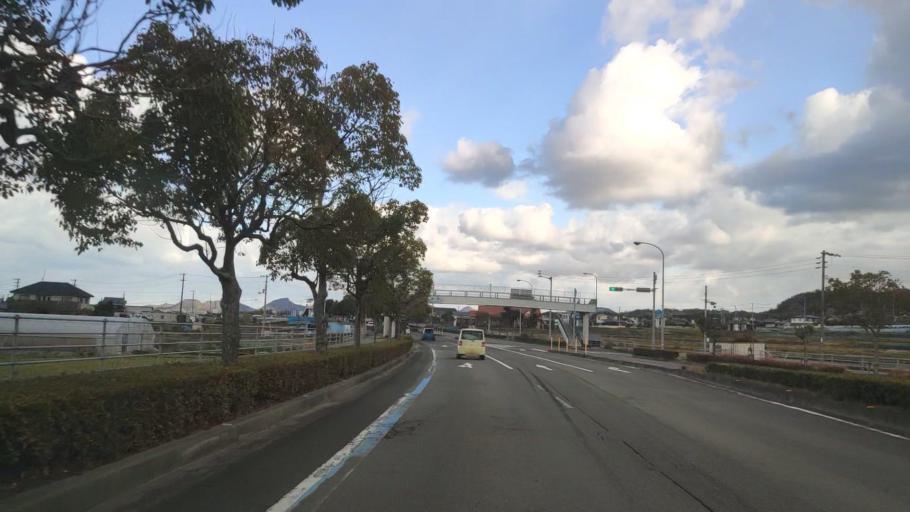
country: JP
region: Ehime
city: Hojo
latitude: 33.9372
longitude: 132.7728
